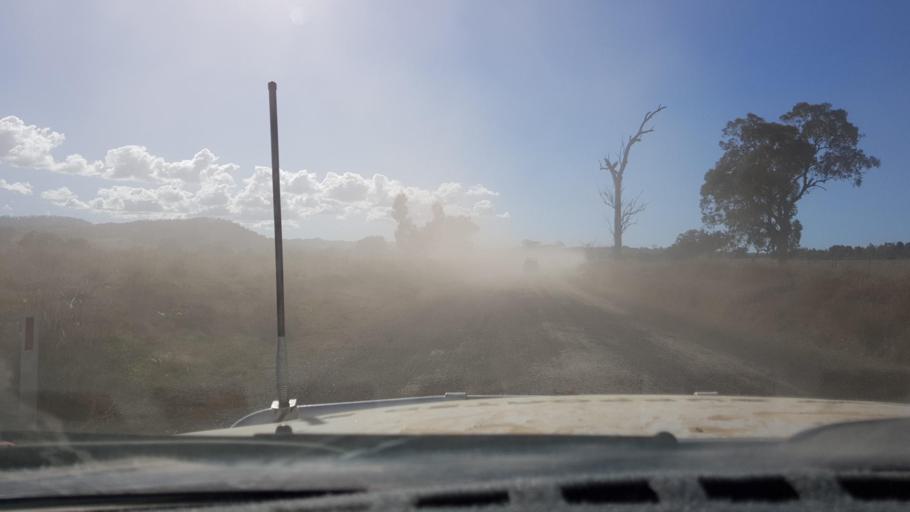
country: AU
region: New South Wales
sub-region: Narrabri
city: Blair Athol
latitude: -30.6734
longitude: 150.4493
